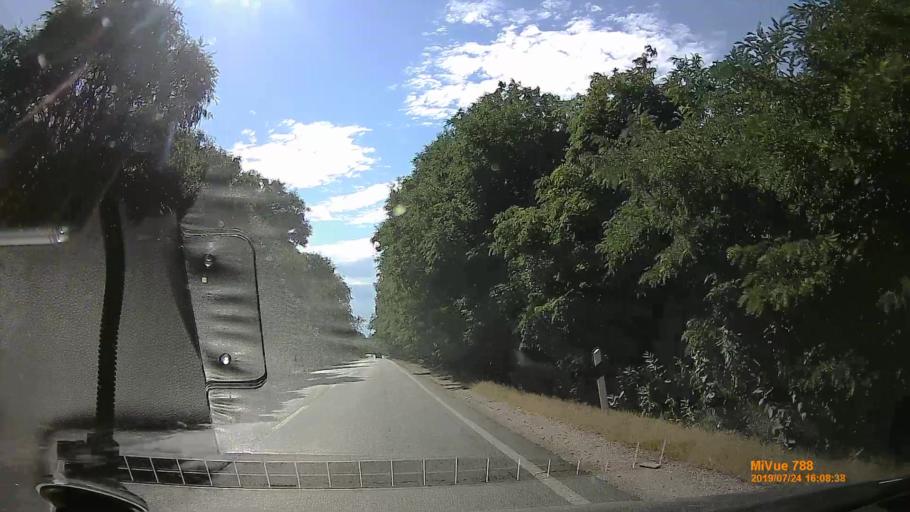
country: HU
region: Szabolcs-Szatmar-Bereg
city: Napkor
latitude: 47.9553
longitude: 21.8871
